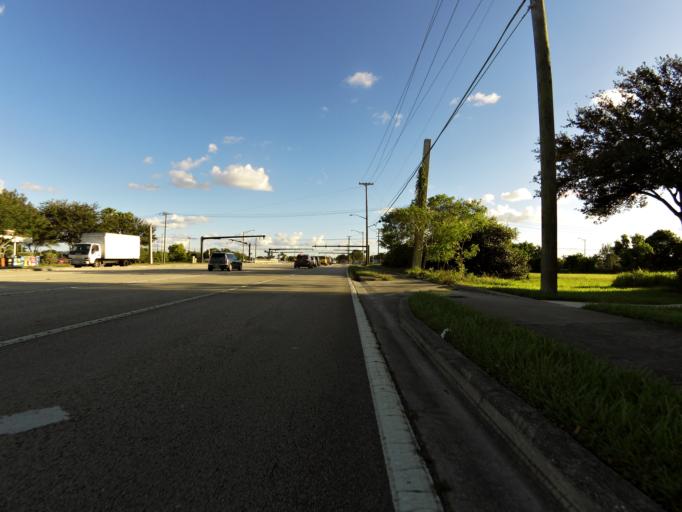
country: US
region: Florida
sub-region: Broward County
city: Cooper City
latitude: 26.0661
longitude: -80.2606
